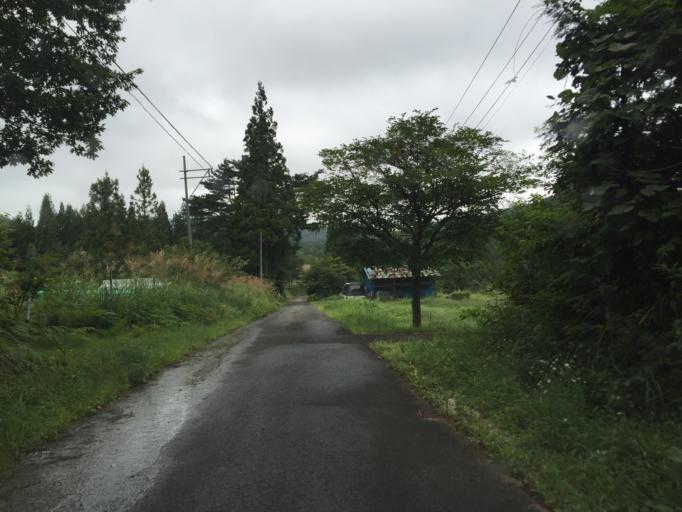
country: JP
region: Fukushima
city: Fukushima-shi
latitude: 37.8111
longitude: 140.3435
